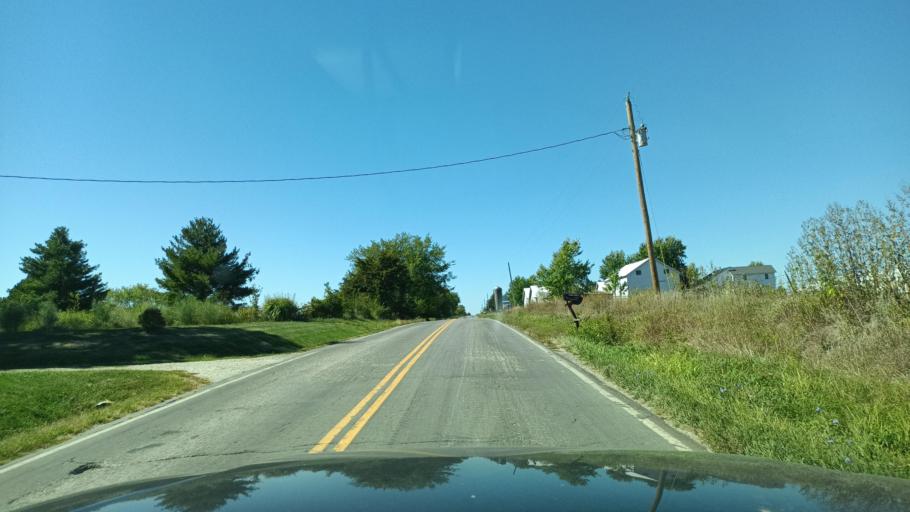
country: US
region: Missouri
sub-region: Macon County
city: La Plata
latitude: 40.0222
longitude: -92.5488
